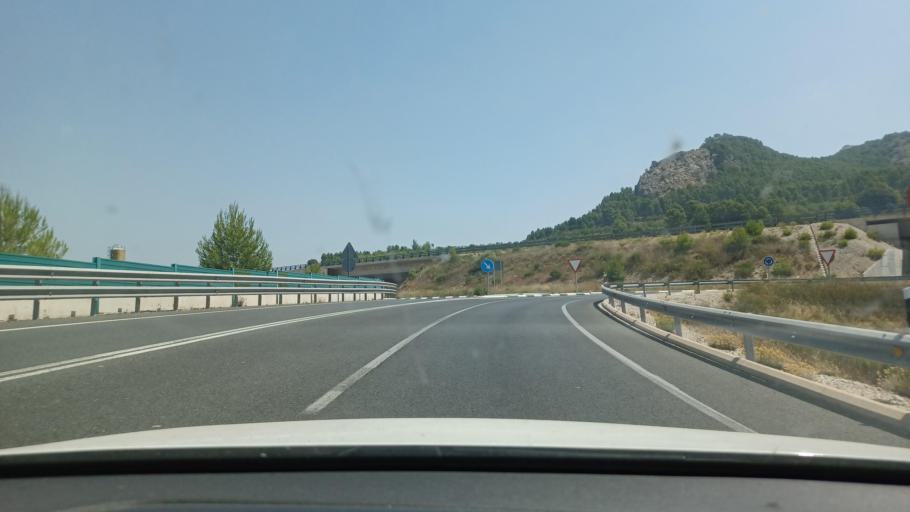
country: ES
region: Valencia
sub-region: Provincia de Alicante
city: Alcoy
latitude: 38.6828
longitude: -0.4623
